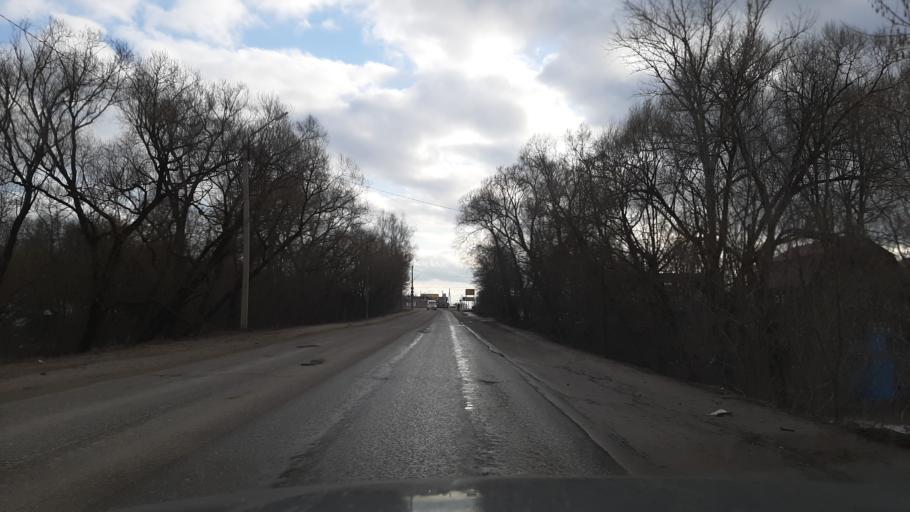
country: RU
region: Ivanovo
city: Teykovo
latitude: 56.8569
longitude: 40.5194
